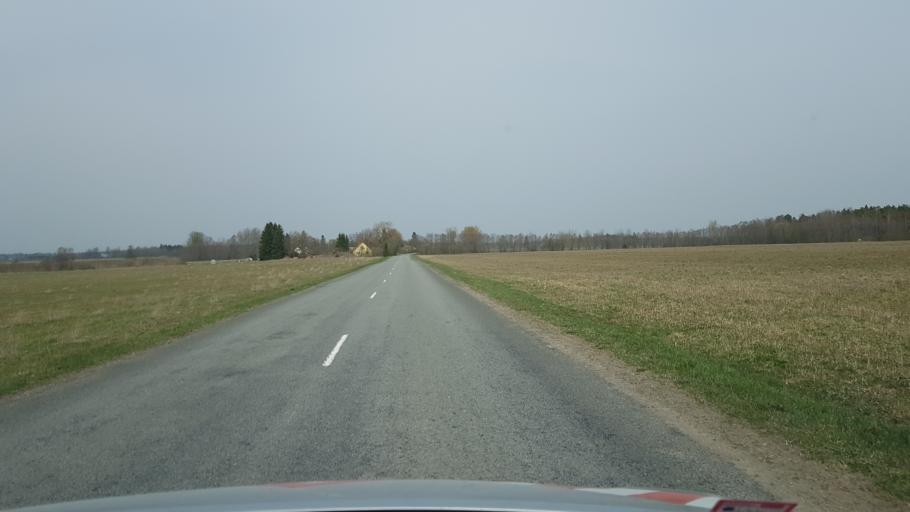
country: EE
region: Harju
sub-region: Kiili vald
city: Kiili
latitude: 59.2804
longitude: 24.8752
